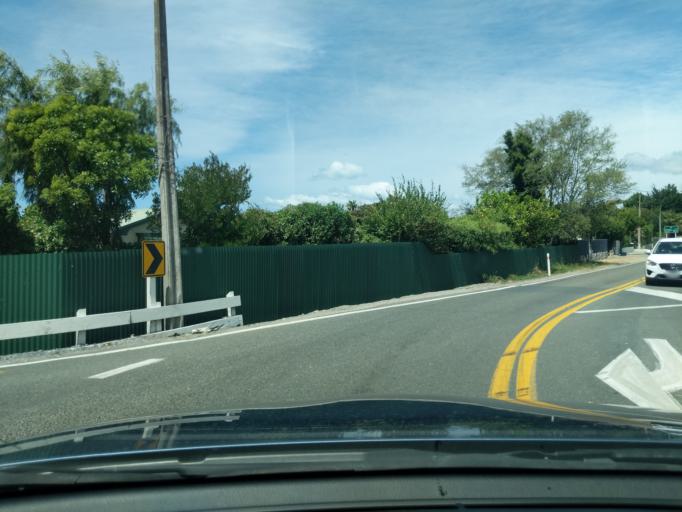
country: NZ
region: Tasman
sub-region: Tasman District
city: Motueka
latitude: -41.0631
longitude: 172.9851
